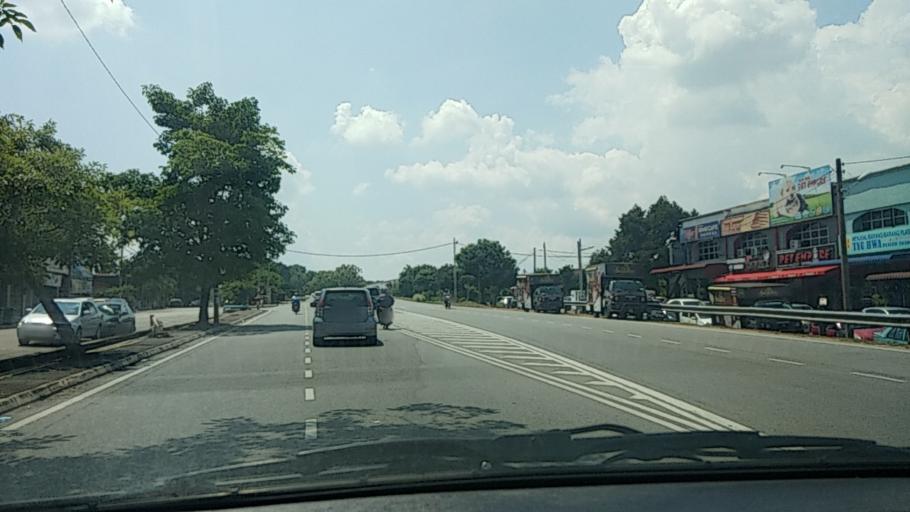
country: MY
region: Kedah
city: Sungai Petani
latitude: 5.6411
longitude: 100.5047
